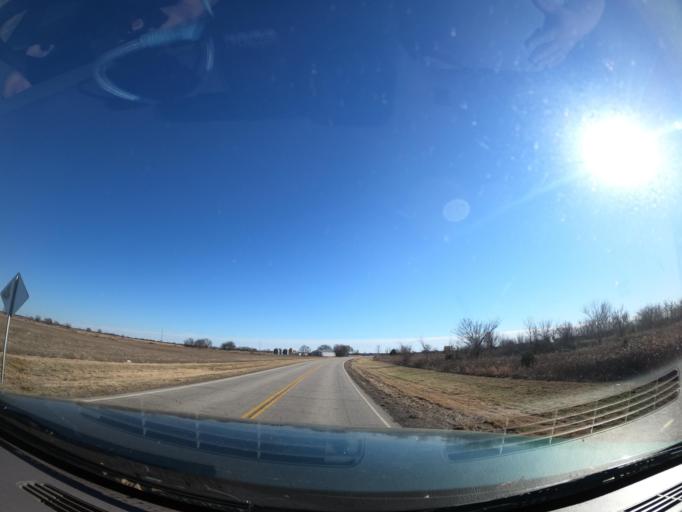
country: US
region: Oklahoma
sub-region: McIntosh County
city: Checotah
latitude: 35.5456
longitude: -95.6479
